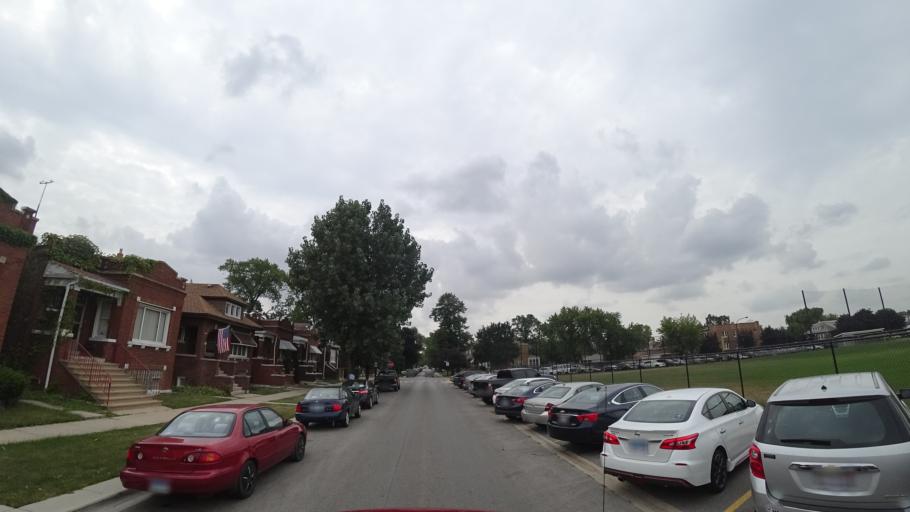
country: US
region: Illinois
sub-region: Cook County
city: Cicero
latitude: 41.8461
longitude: -87.7699
